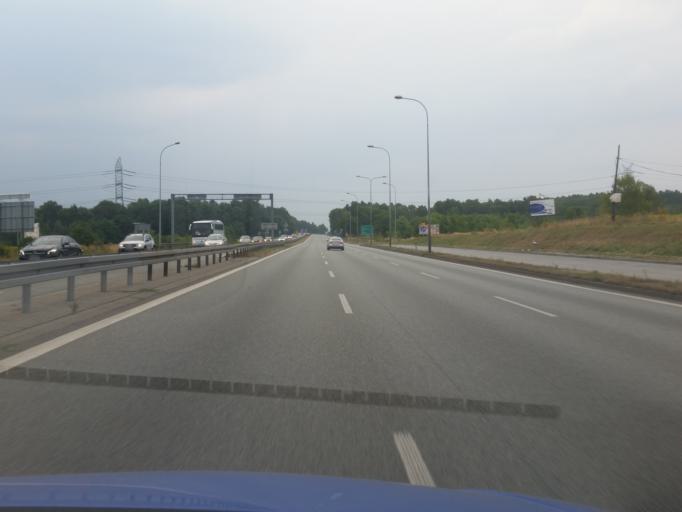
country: PL
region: Silesian Voivodeship
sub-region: Powiat bedzinski
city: Siewierz
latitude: 50.4283
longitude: 19.2147
